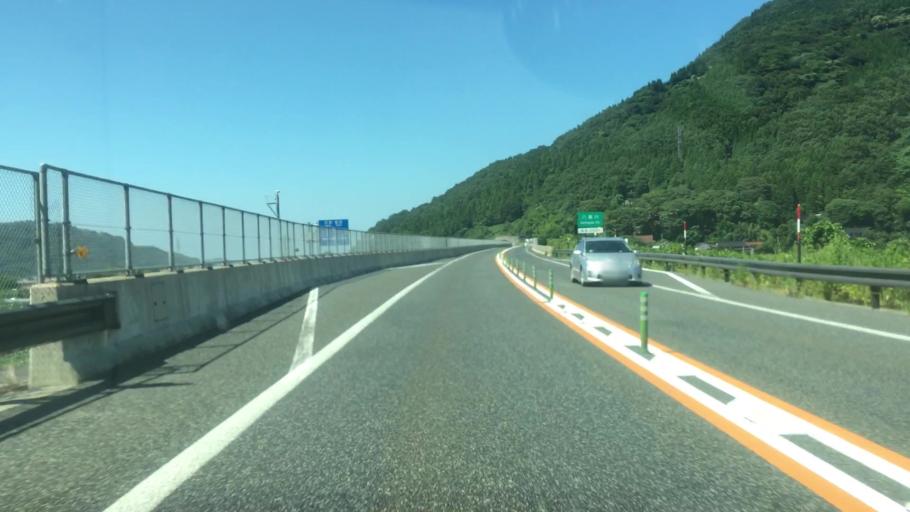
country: JP
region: Tottori
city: Tottori
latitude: 35.4042
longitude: 134.2054
